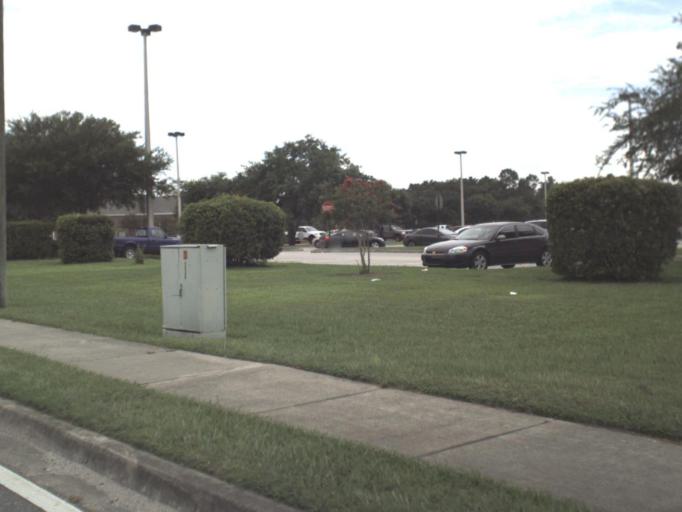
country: US
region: Florida
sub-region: Citrus County
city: Crystal River
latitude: 28.8908
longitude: -82.5481
